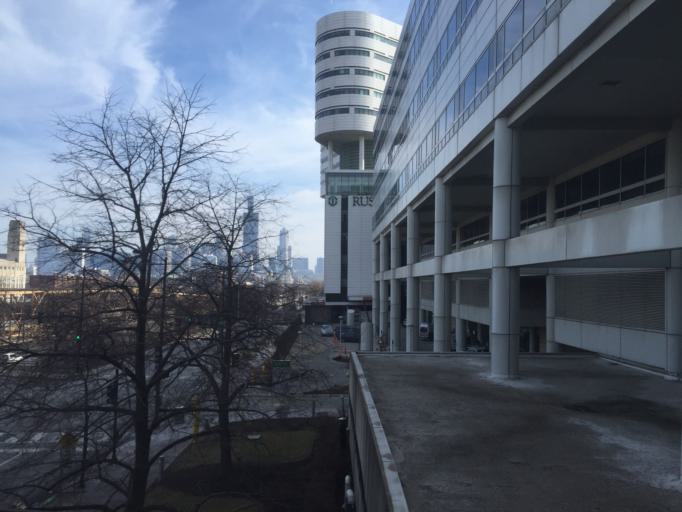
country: US
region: Illinois
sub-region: Cook County
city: Chicago
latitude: 41.8750
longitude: -87.6698
